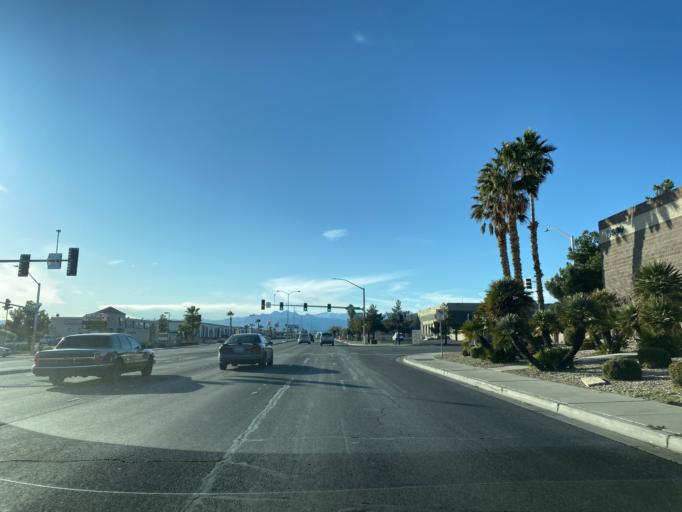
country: US
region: Nevada
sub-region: Clark County
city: Nellis Air Force Base
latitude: 36.2404
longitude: -115.0886
